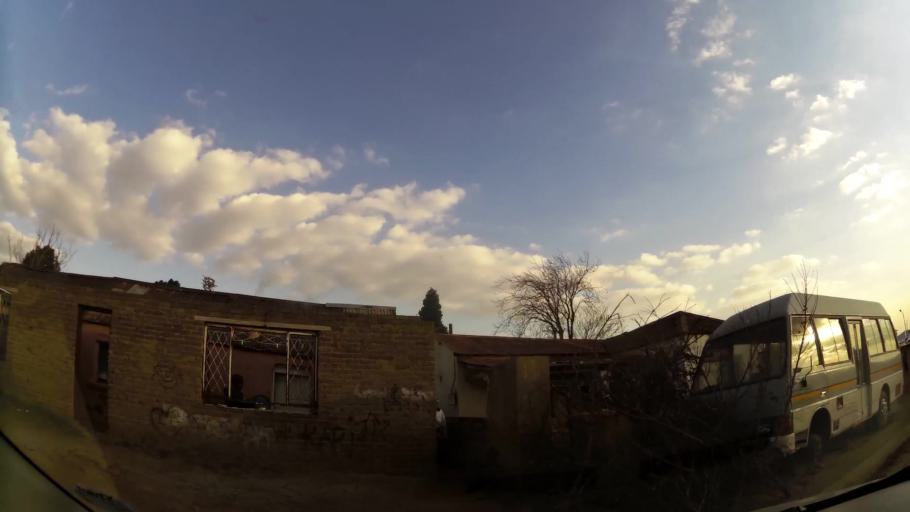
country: ZA
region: Gauteng
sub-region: West Rand District Municipality
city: Krugersdorp
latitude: -26.0761
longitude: 27.7585
